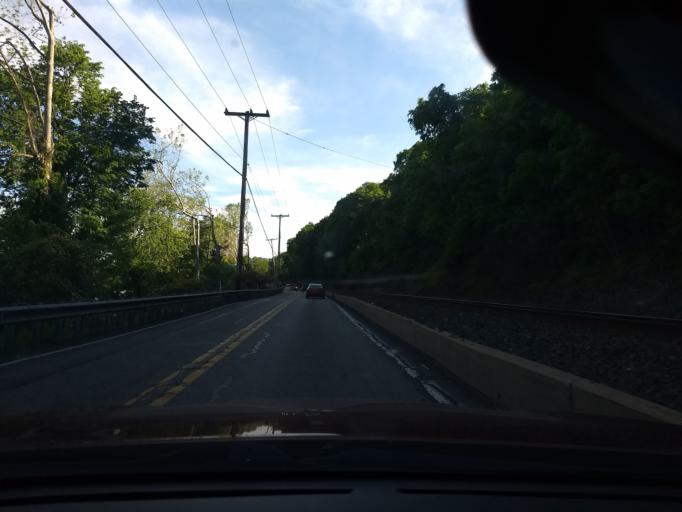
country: US
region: Pennsylvania
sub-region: Allegheny County
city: Glassport
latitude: 40.3281
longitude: -79.8984
